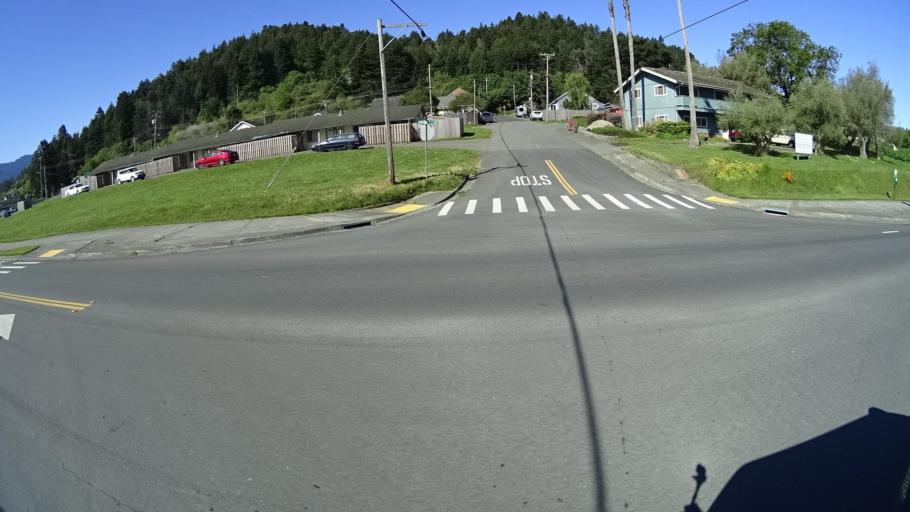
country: US
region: California
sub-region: Humboldt County
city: Rio Dell
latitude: 40.5025
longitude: -124.1070
